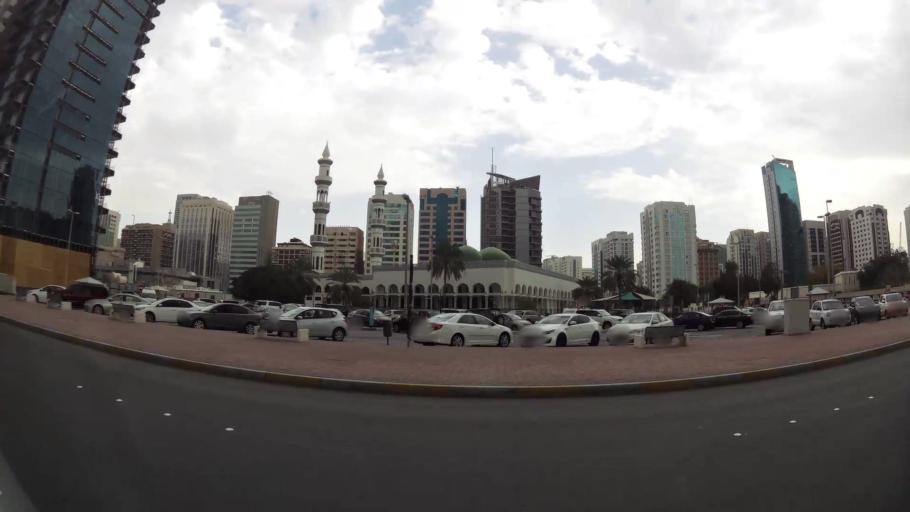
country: AE
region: Abu Dhabi
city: Abu Dhabi
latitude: 24.4857
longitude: 54.3512
